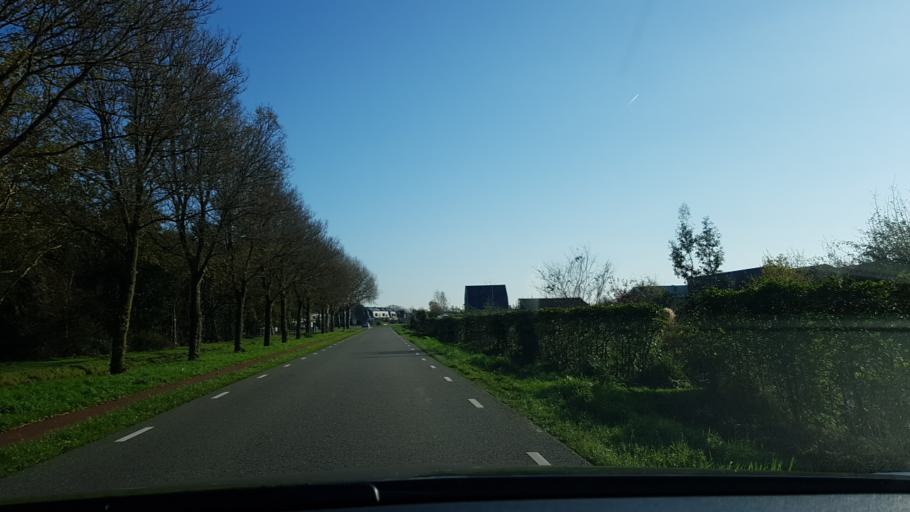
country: NL
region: North Holland
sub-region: Gemeente Uitgeest
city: Uitgeest
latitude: 52.4671
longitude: 4.7312
